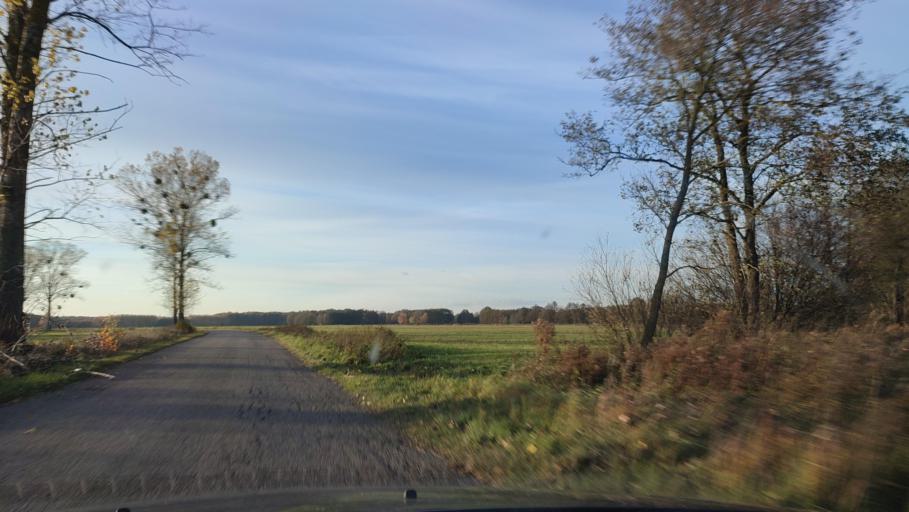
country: PL
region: Masovian Voivodeship
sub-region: Powiat przasnyski
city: Krzynowloga Mala
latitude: 53.3316
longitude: 20.7202
